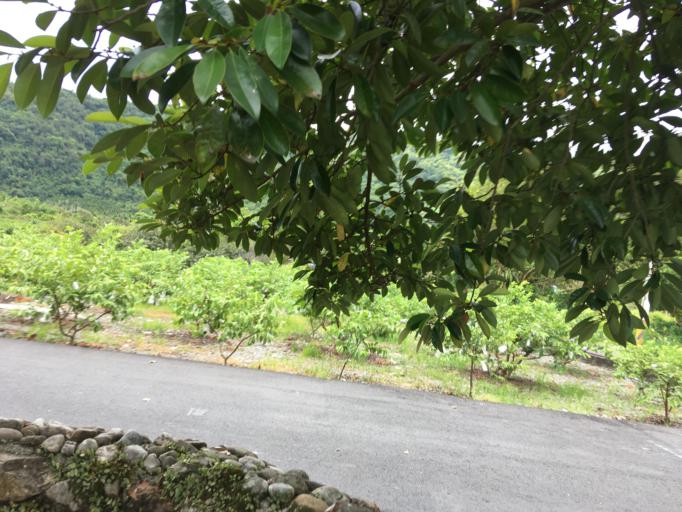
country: TW
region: Taiwan
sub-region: Yilan
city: Yilan
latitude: 24.6336
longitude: 121.7160
